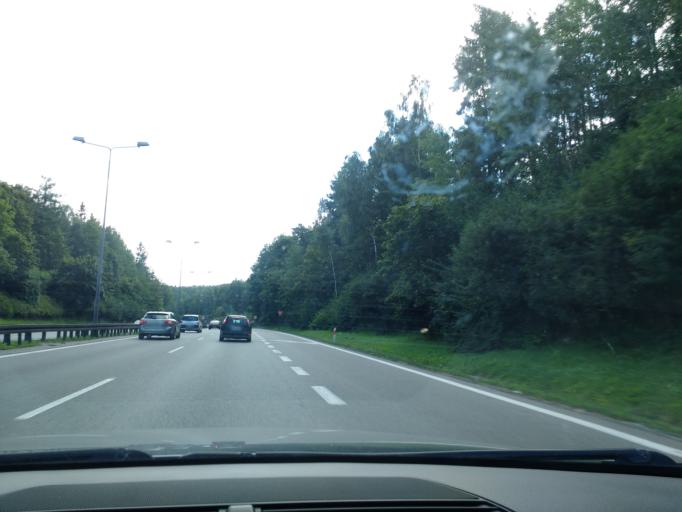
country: PL
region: Pomeranian Voivodeship
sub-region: Gdynia
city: Wielki Kack
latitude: 54.4970
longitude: 18.4619
